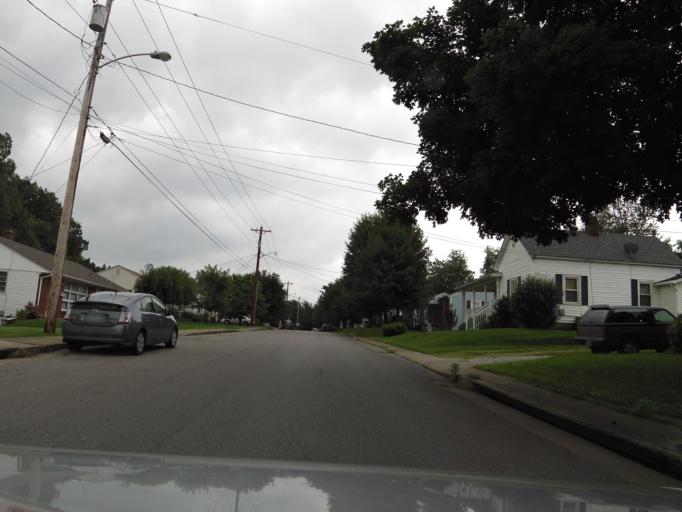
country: US
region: Kentucky
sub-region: Hopkins County
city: Madisonville
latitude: 37.3194
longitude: -87.4968
